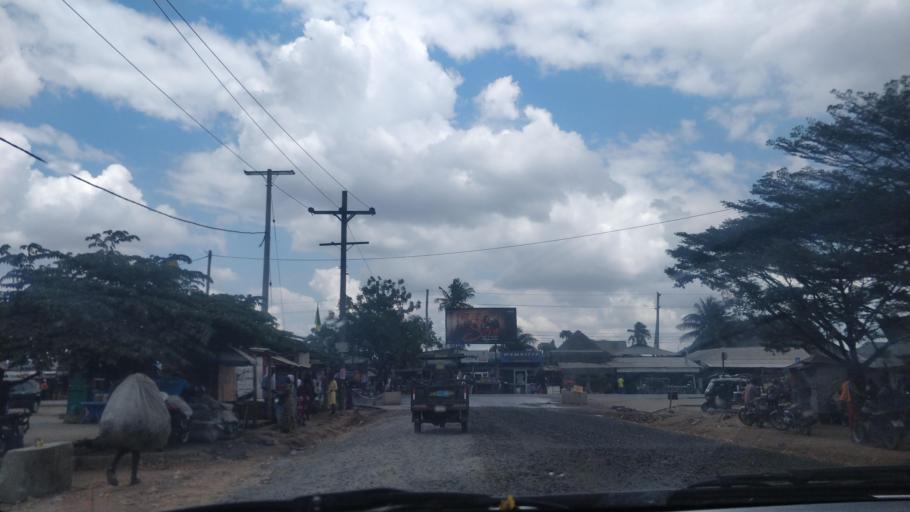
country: TZ
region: Dar es Salaam
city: Magomeni
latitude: -6.8087
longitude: 39.2221
